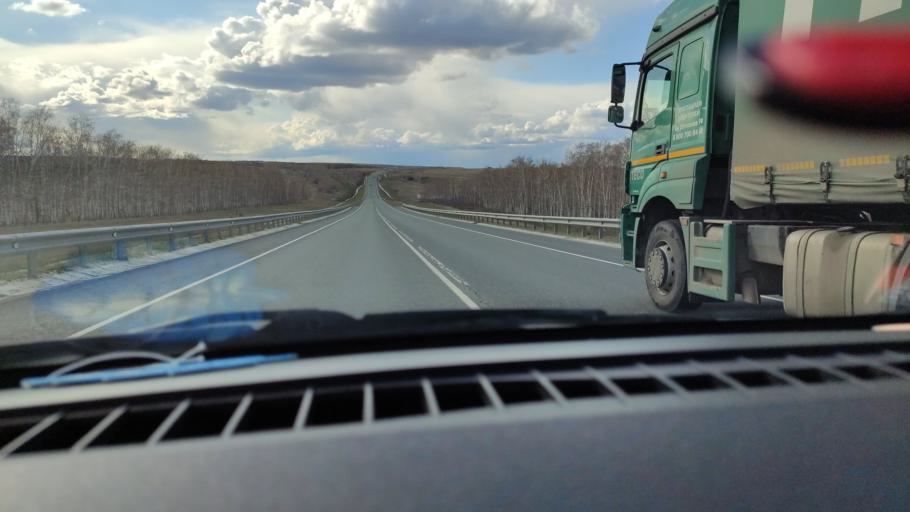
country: RU
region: Saratov
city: Shikhany
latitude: 52.1258
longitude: 47.2448
